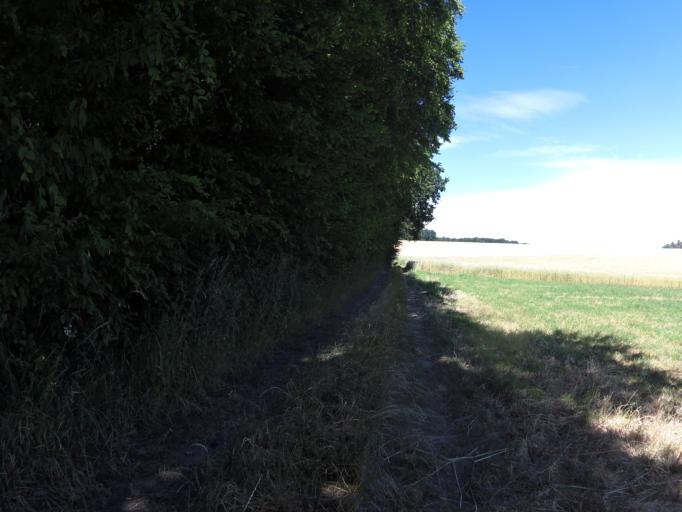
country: DE
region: Bavaria
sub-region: Regierungsbezirk Unterfranken
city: Geroldshausen
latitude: 49.7045
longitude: 9.8817
